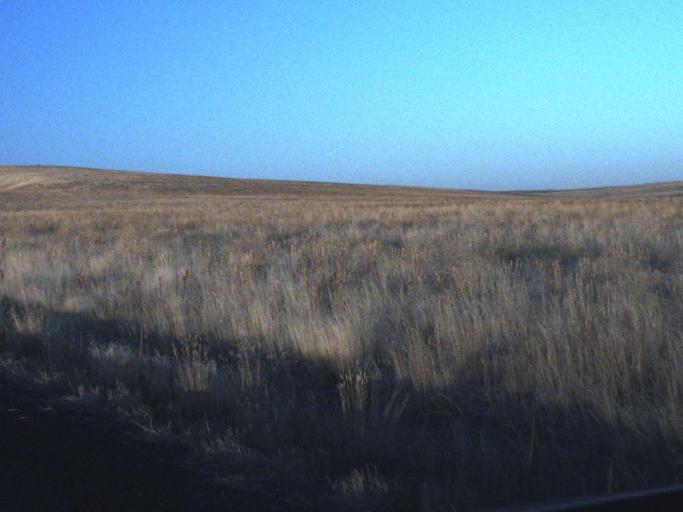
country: US
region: Washington
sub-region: Adams County
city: Ritzville
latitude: 46.9773
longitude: -118.6638
